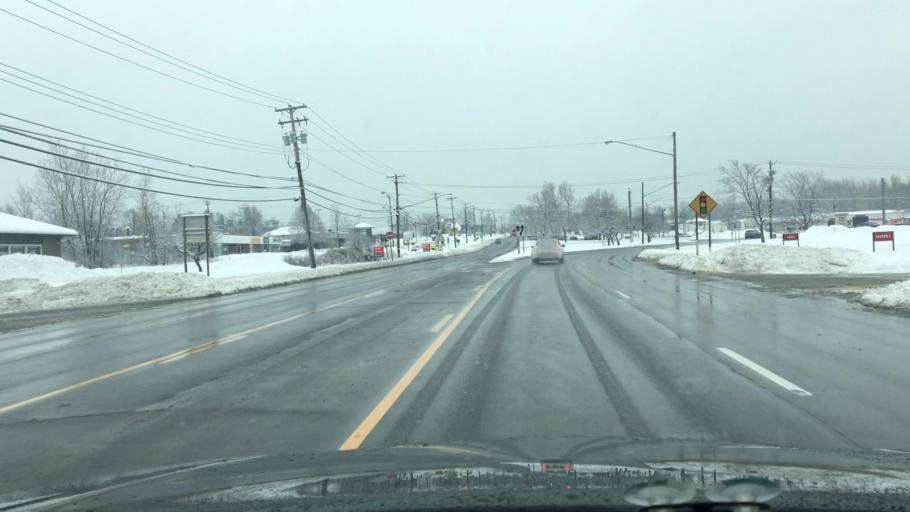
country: US
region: New York
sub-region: Erie County
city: Orchard Park
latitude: 42.8023
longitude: -78.7518
